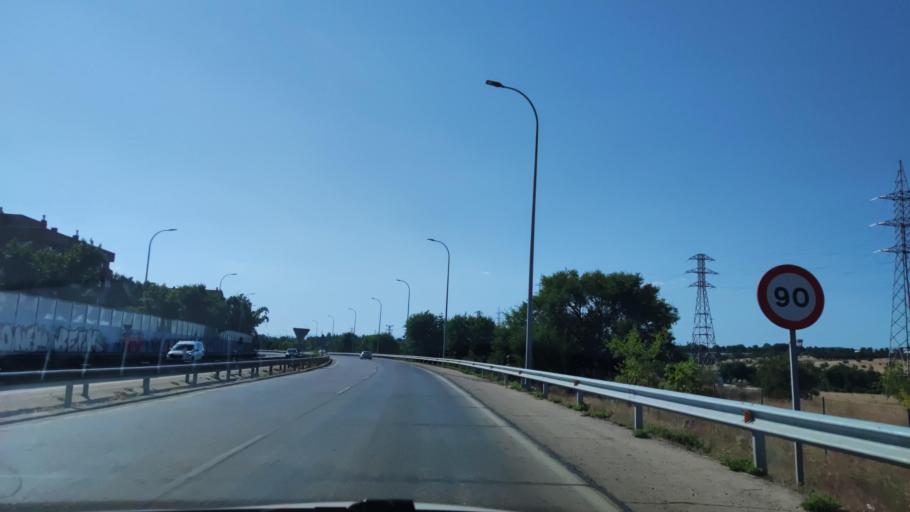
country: ES
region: Madrid
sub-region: Provincia de Madrid
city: Alcorcon
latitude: 40.3545
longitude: -3.7992
